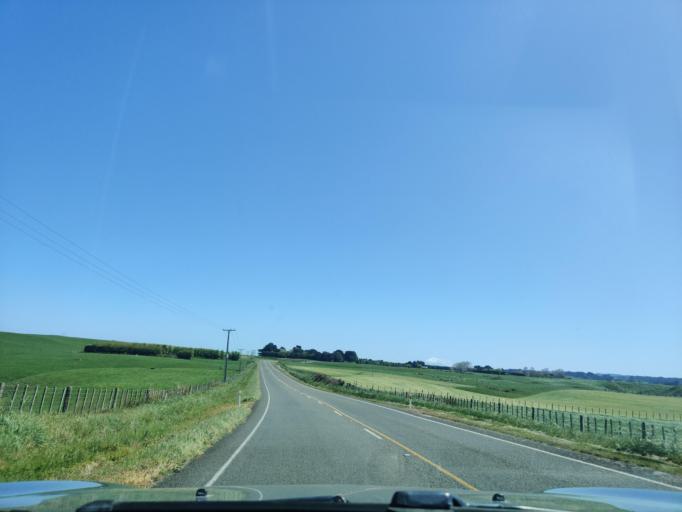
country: NZ
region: Taranaki
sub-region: South Taranaki District
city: Patea
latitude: -39.7976
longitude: 174.7130
